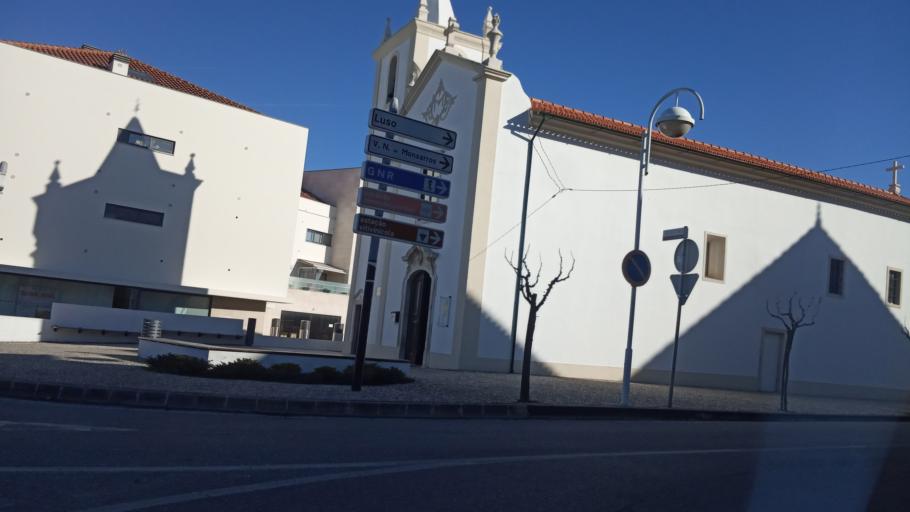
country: PT
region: Aveiro
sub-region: Anadia
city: Anadia
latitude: 40.4418
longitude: -8.4370
